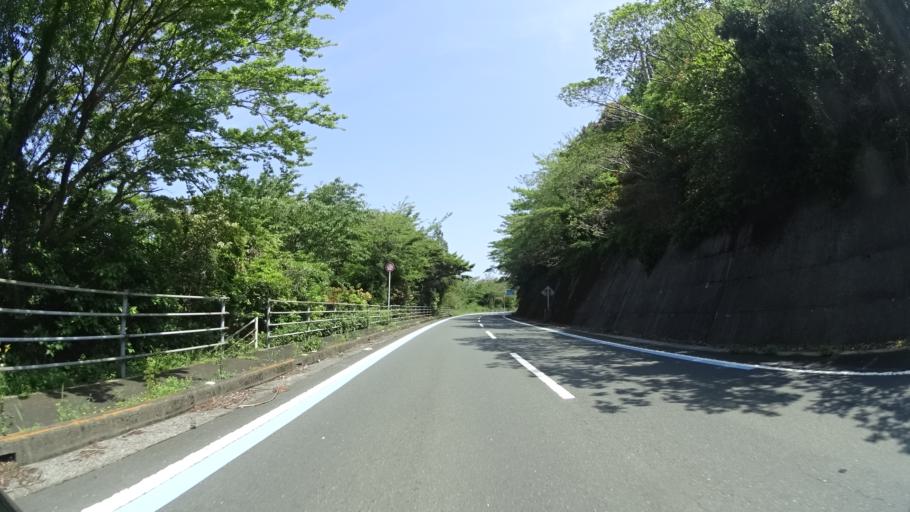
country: JP
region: Ehime
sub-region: Nishiuwa-gun
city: Ikata-cho
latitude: 33.4134
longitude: 132.1724
